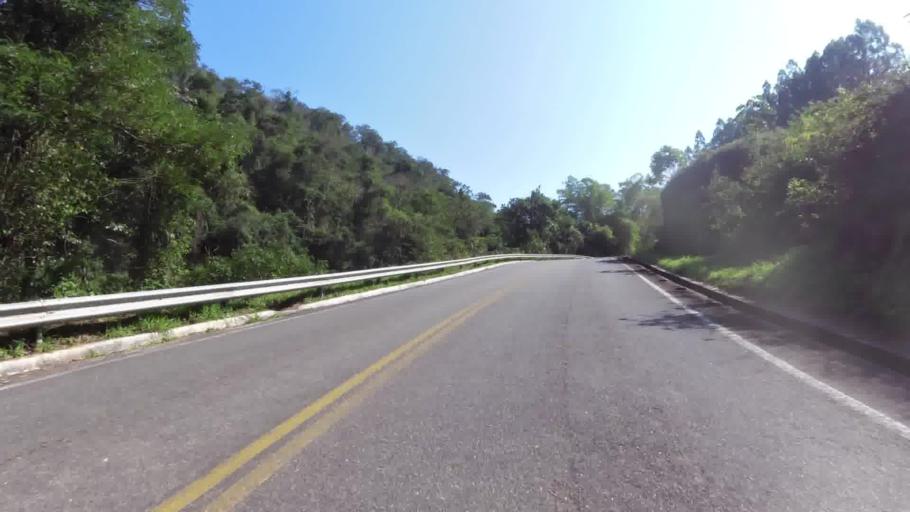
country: BR
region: Espirito Santo
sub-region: Alfredo Chaves
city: Alfredo Chaves
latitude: -20.5740
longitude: -40.8068
